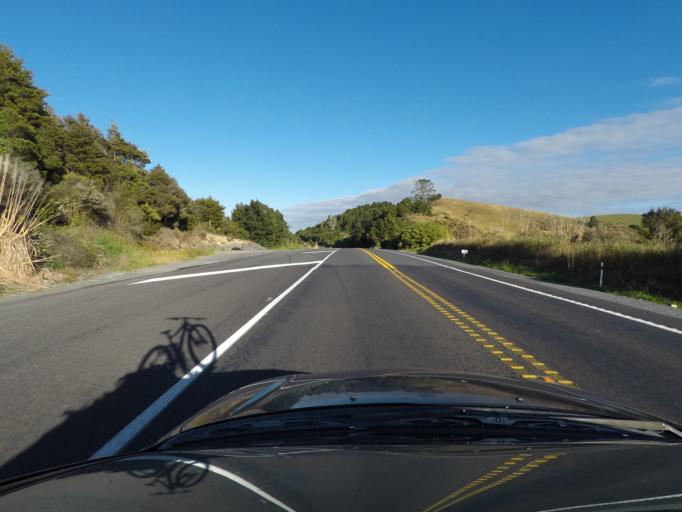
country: NZ
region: Northland
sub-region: Far North District
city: Kawakawa
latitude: -35.4817
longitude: 174.1199
